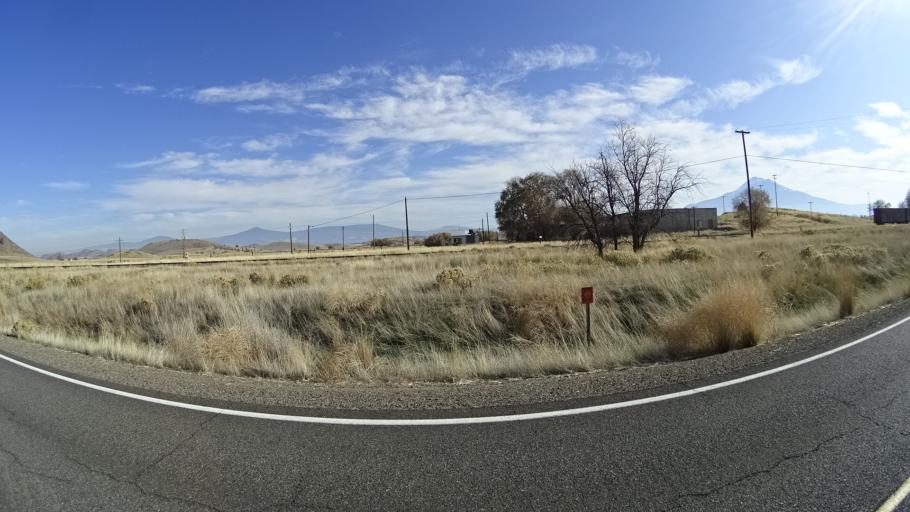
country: US
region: California
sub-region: Siskiyou County
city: Weed
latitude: 41.5273
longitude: -122.5222
